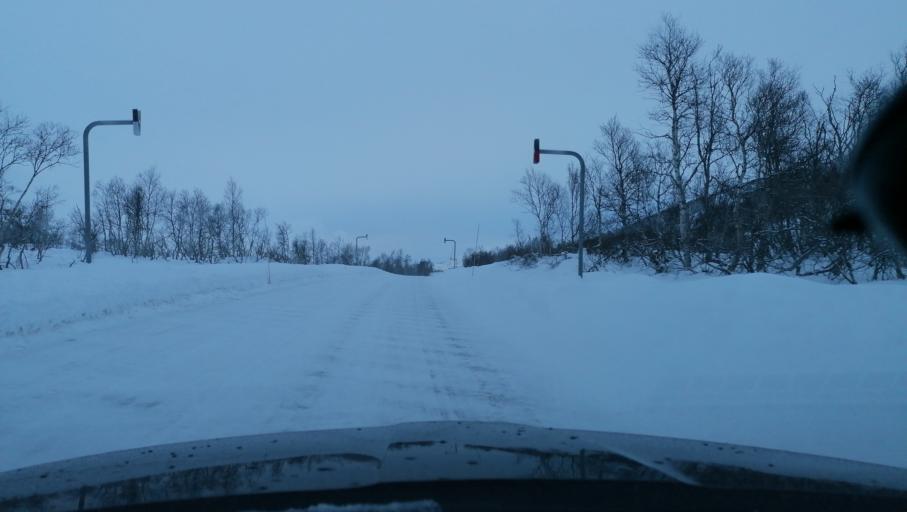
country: NO
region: Aust-Agder
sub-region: Bykle
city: Hovden
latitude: 59.6333
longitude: 7.4535
